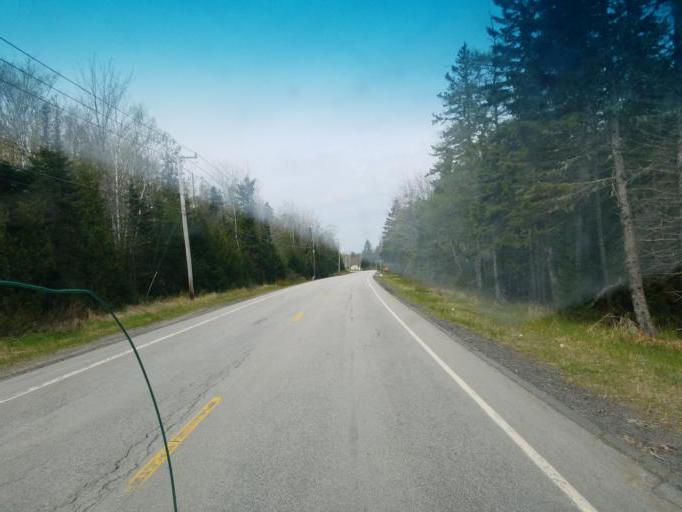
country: US
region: Maine
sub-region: Washington County
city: Eastport
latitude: 44.8012
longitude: -67.1323
